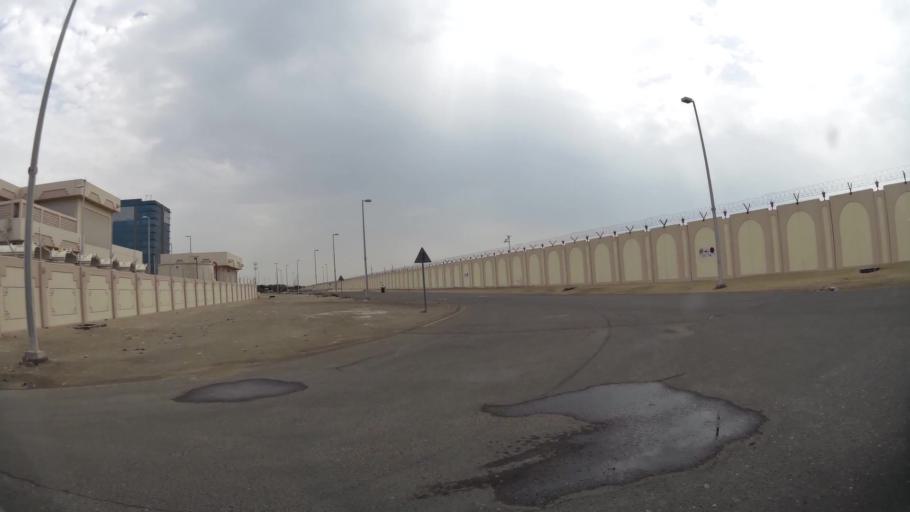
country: AE
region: Abu Dhabi
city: Abu Dhabi
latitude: 24.4301
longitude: 54.4588
